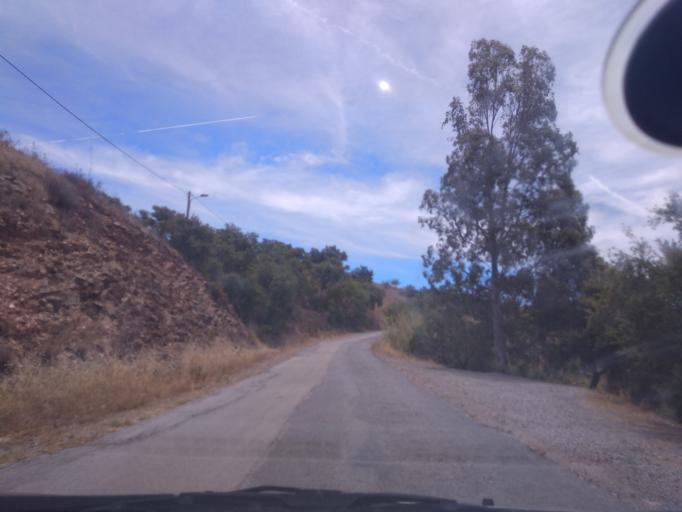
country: PT
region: Faro
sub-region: Sao Bras de Alportel
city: Sao Bras de Alportel
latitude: 37.1757
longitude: -7.8068
